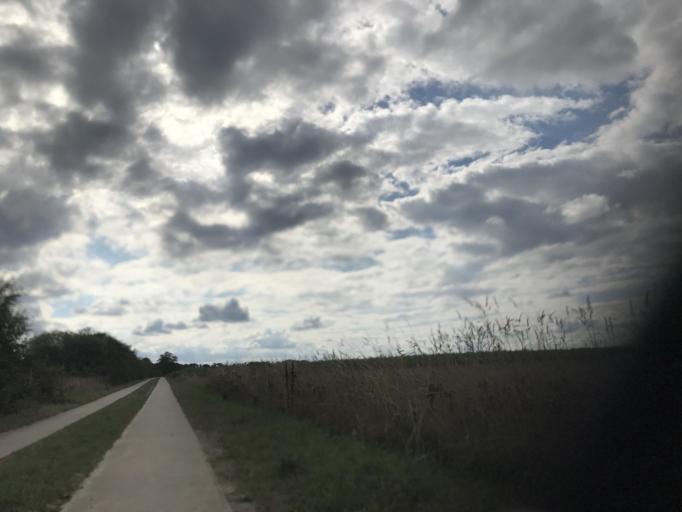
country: DE
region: Lower Saxony
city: Reinstorf
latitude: 53.2554
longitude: 10.5822
